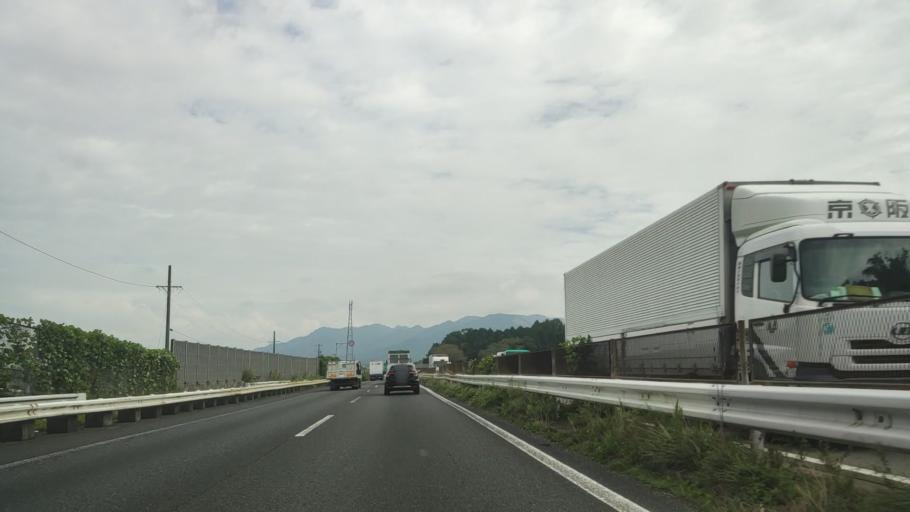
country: JP
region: Mie
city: Ueno-ebisumachi
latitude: 34.8255
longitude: 136.2299
